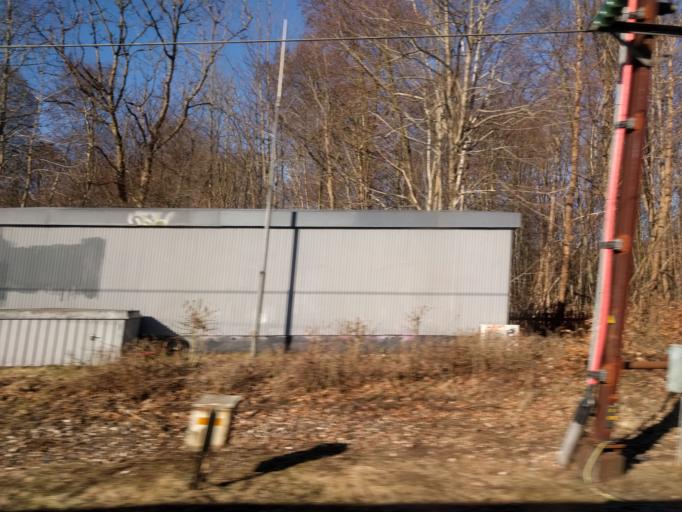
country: DK
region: Capital Region
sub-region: Rudersdal Kommune
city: Trorod
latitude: 55.8247
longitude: 12.5714
